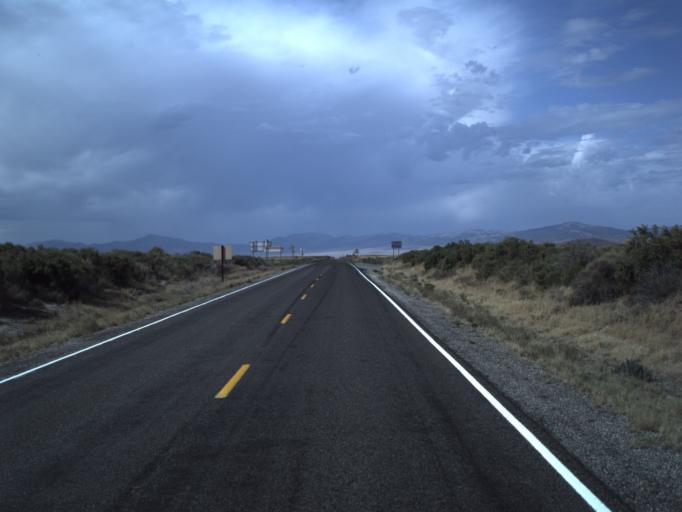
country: US
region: Nevada
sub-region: Elko County
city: West Wendover
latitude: 41.3688
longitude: -114.0383
